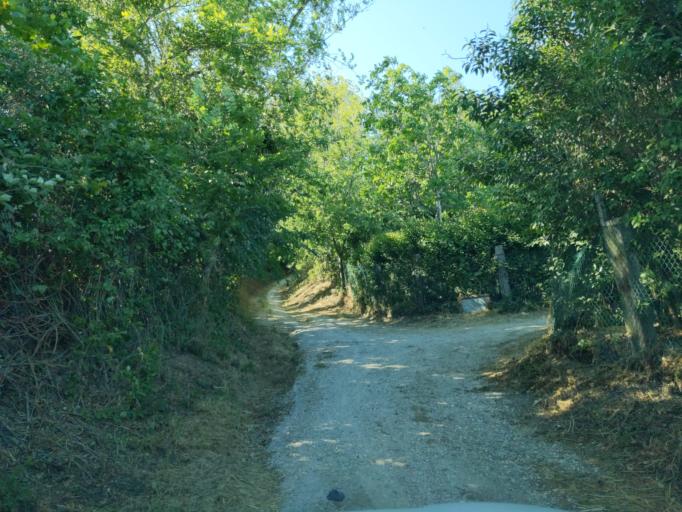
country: IT
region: The Marches
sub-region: Provincia di Pesaro e Urbino
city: Cuccurano
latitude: 43.8029
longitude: 12.9628
